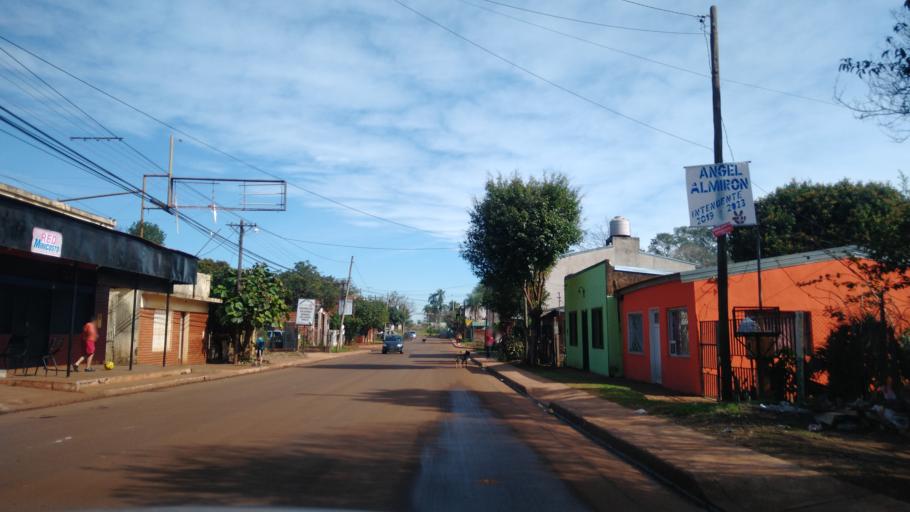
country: AR
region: Misiones
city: Garupa
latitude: -27.4659
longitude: -55.8609
